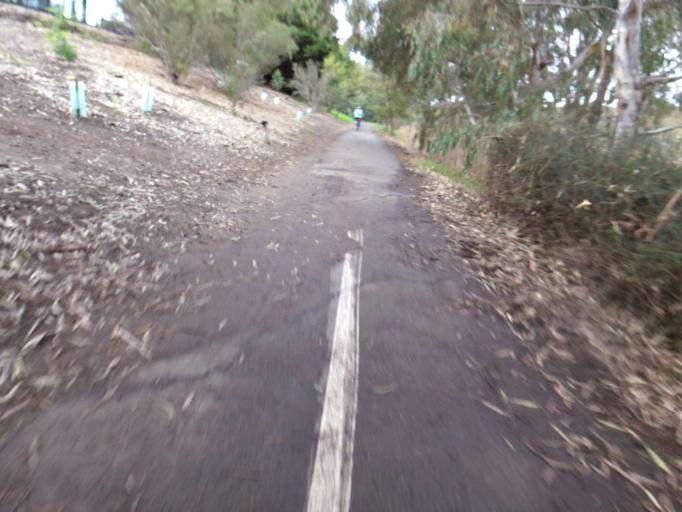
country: AU
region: Victoria
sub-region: Greater Geelong
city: Wandana Heights
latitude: -38.1612
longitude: 144.3241
